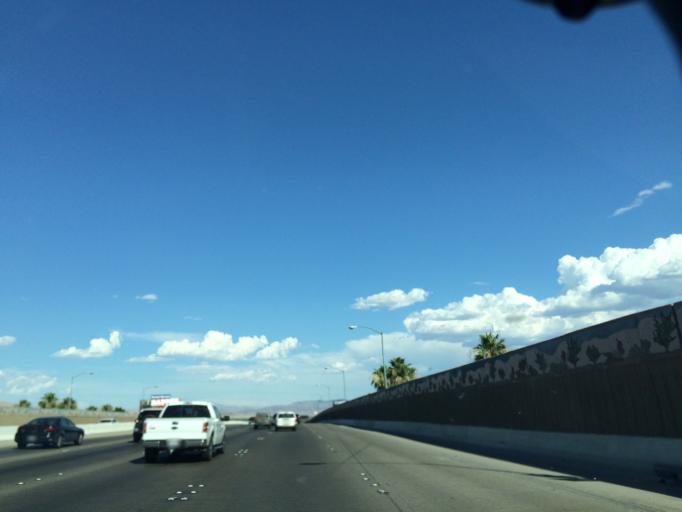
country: US
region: Nevada
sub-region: Clark County
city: Las Vegas
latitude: 36.1710
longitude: -115.1323
